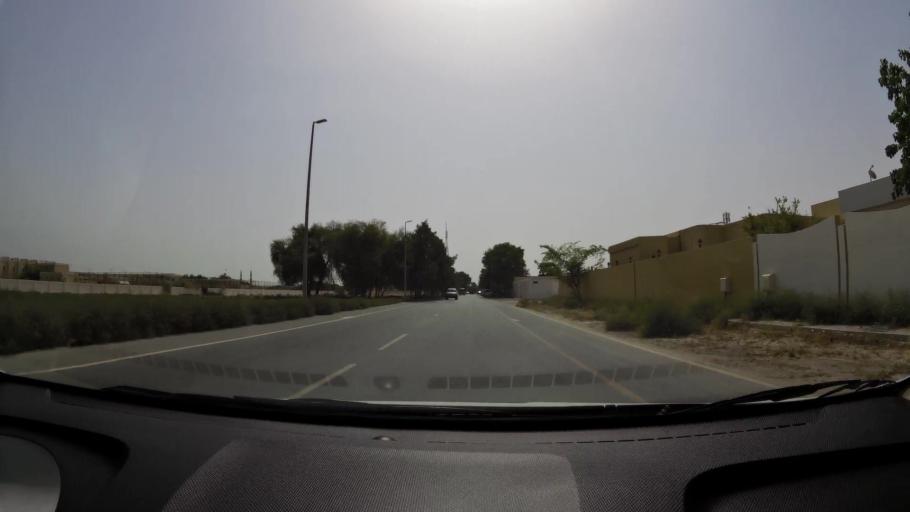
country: AE
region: Ash Shariqah
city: Sharjah
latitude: 25.3521
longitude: 55.4208
